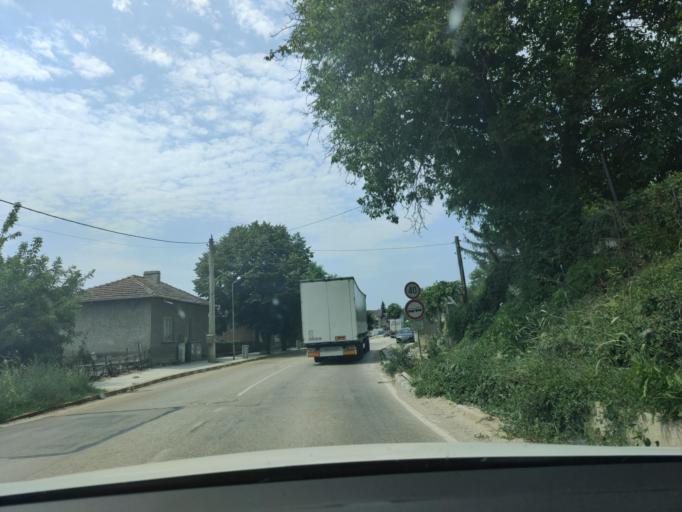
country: BG
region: Vidin
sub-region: Obshtina Dimovo
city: Dimovo
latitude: 43.7483
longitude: 22.7351
